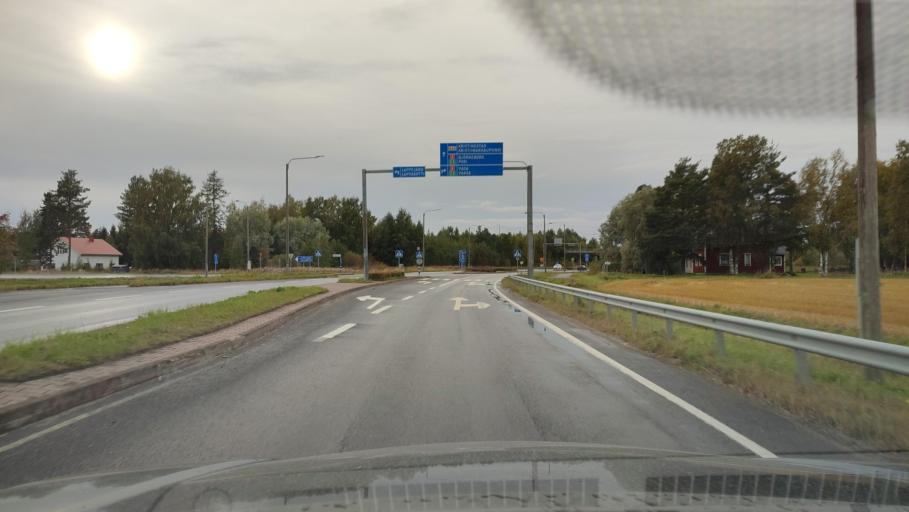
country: FI
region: Ostrobothnia
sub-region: Sydosterbotten
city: Kristinestad
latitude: 62.2602
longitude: 21.4925
